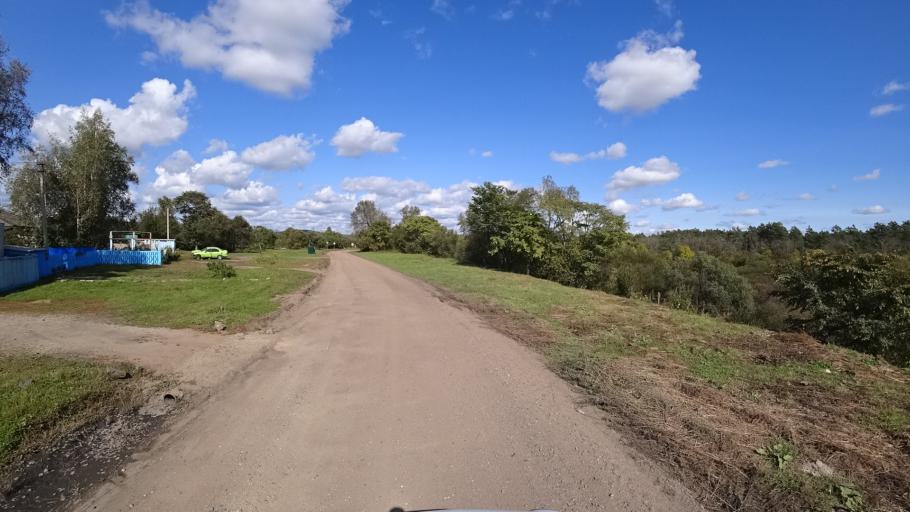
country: RU
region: Amur
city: Arkhara
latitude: 49.4049
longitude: 130.1563
